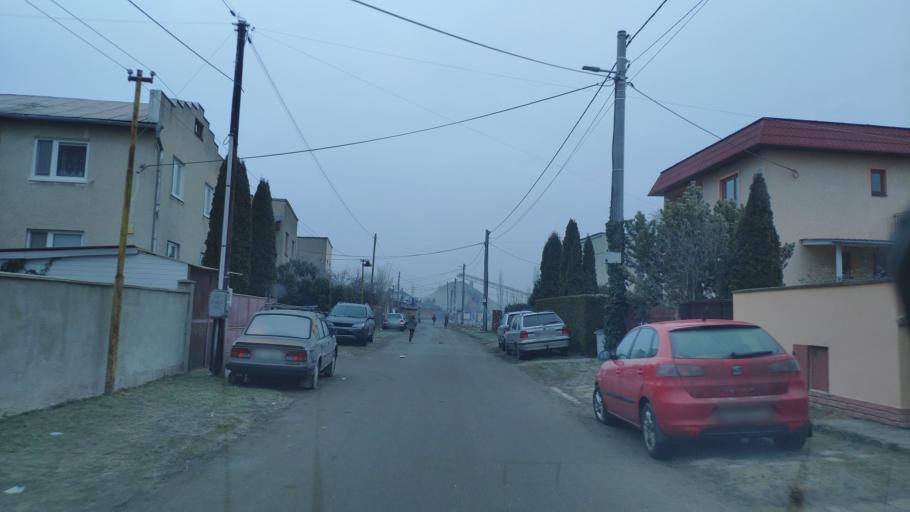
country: SK
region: Kosicky
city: Kosice
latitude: 48.6180
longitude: 21.3190
